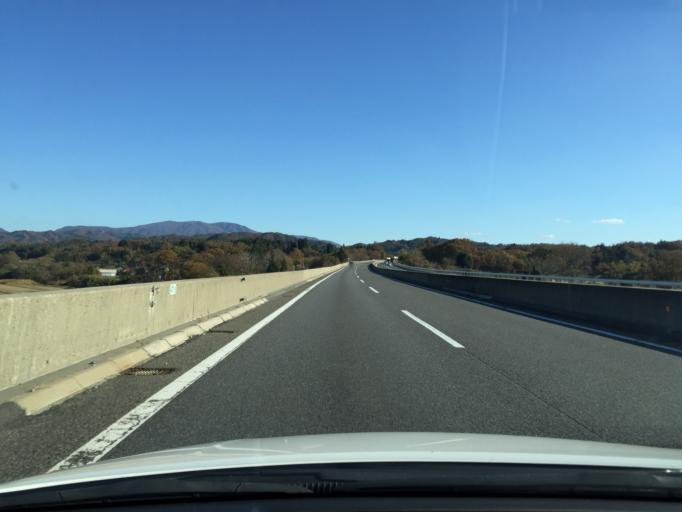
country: JP
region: Fukushima
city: Funehikimachi-funehiki
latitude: 37.3942
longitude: 140.5865
